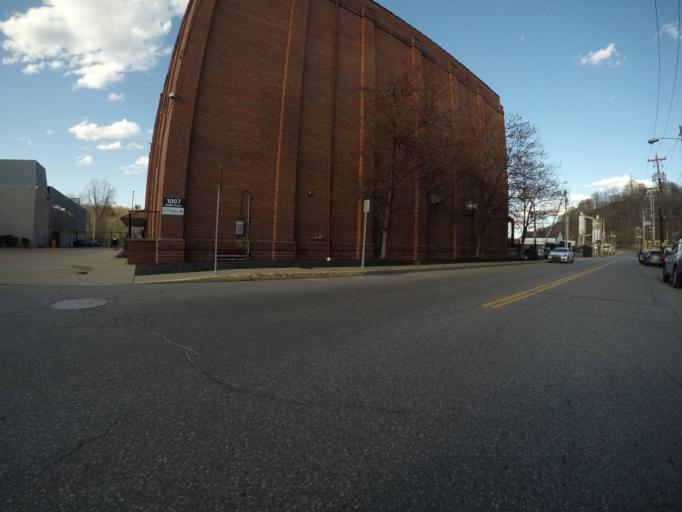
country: US
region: West Virginia
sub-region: Kanawha County
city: Charleston
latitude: 38.3568
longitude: -81.6287
